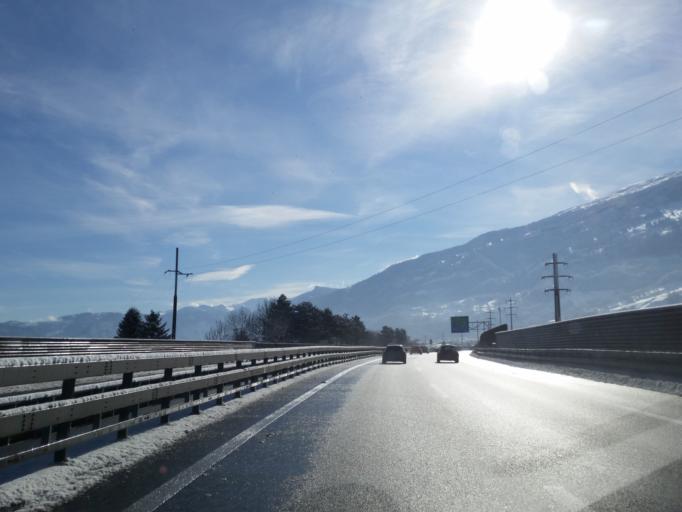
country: CH
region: Saint Gallen
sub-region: Wahlkreis Sarganserland
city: Sargans
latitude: 47.0503
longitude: 9.4293
